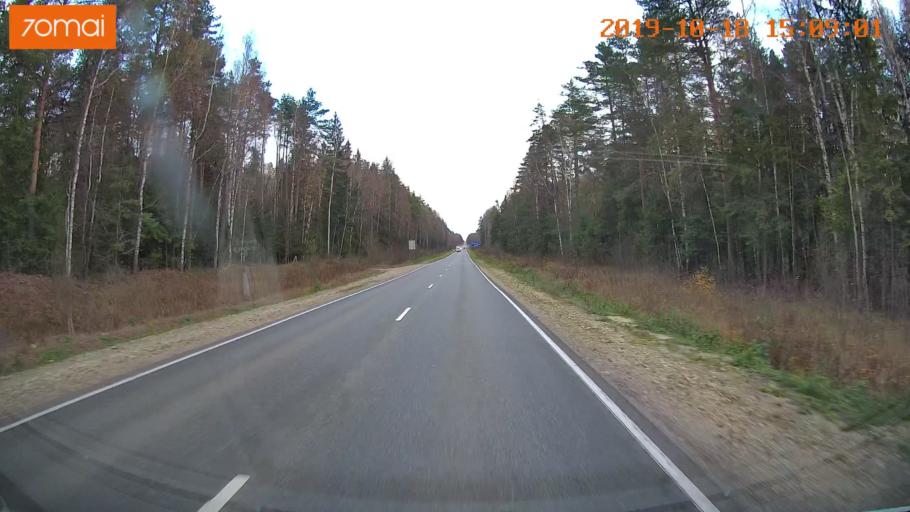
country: RU
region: Vladimir
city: Gus'-Khrustal'nyy
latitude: 55.5604
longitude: 40.6167
